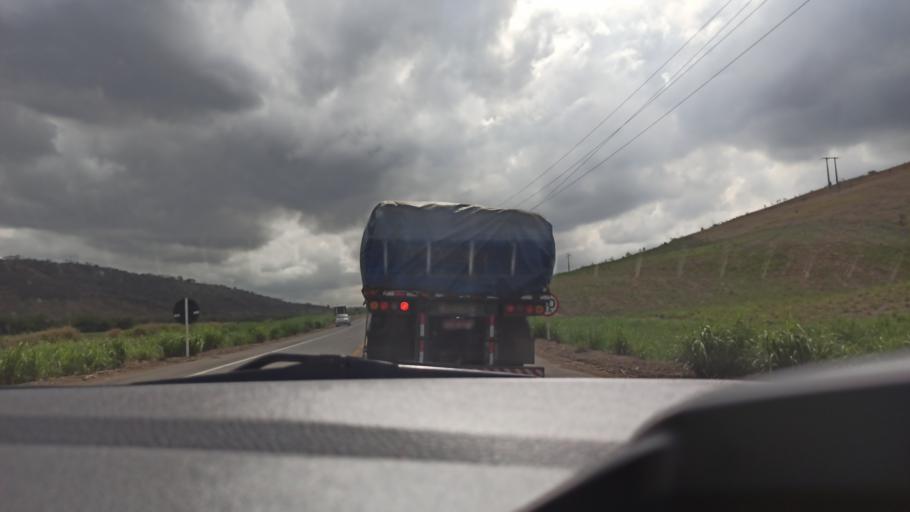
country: BR
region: Pernambuco
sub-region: Timbauba
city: Timbauba
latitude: -7.5226
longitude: -35.2978
